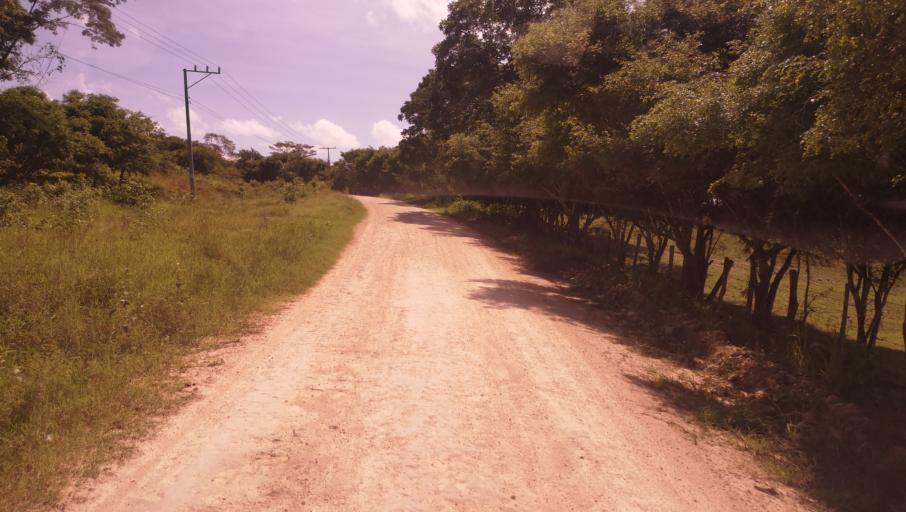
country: GT
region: Peten
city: Melchor de Mencos
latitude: 16.9274
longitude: -89.2799
